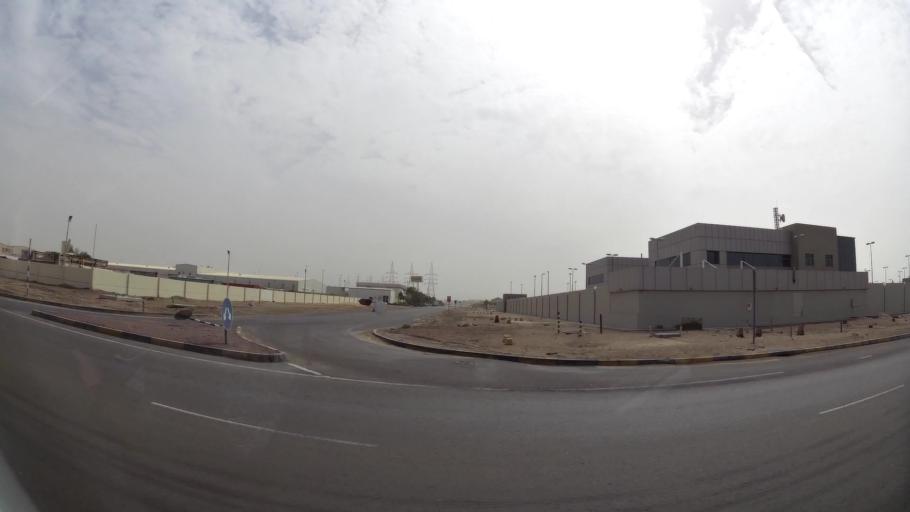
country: AE
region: Abu Dhabi
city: Abu Dhabi
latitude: 24.3236
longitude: 54.5100
